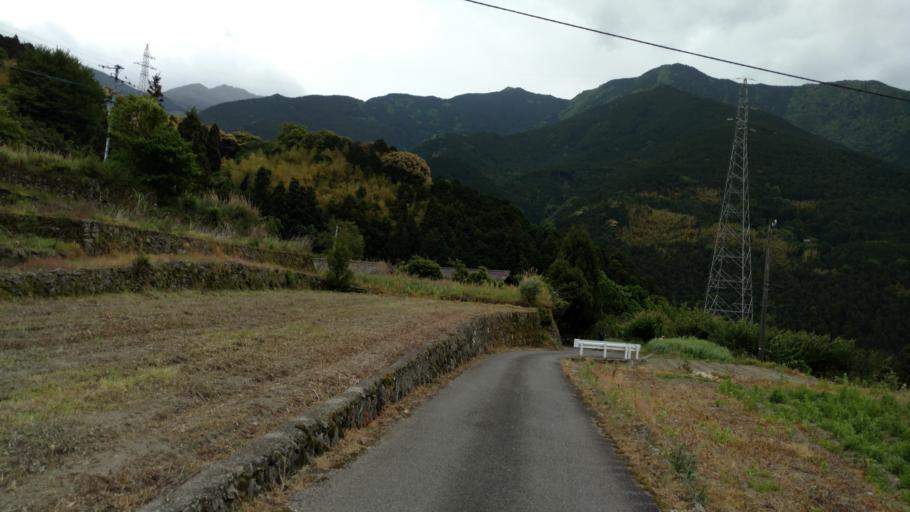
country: JP
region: Ehime
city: Saijo
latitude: 33.8626
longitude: 133.1965
